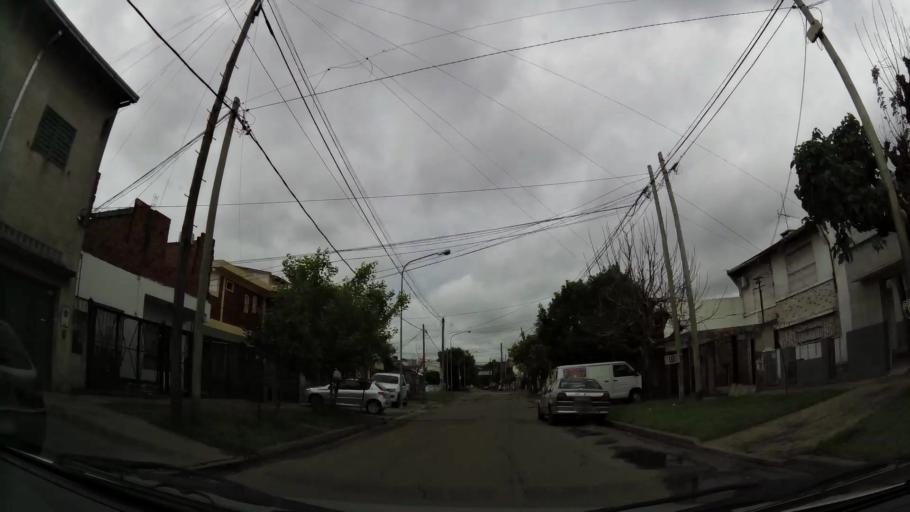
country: AR
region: Buenos Aires
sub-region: Partido de Lanus
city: Lanus
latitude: -34.7265
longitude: -58.3751
